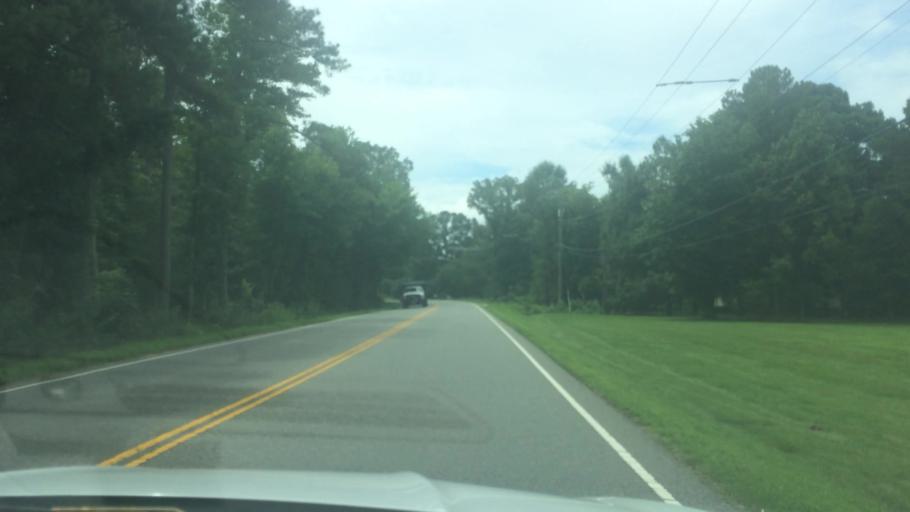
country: US
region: Virginia
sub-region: James City County
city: Williamsburg
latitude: 37.2586
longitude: -76.7646
